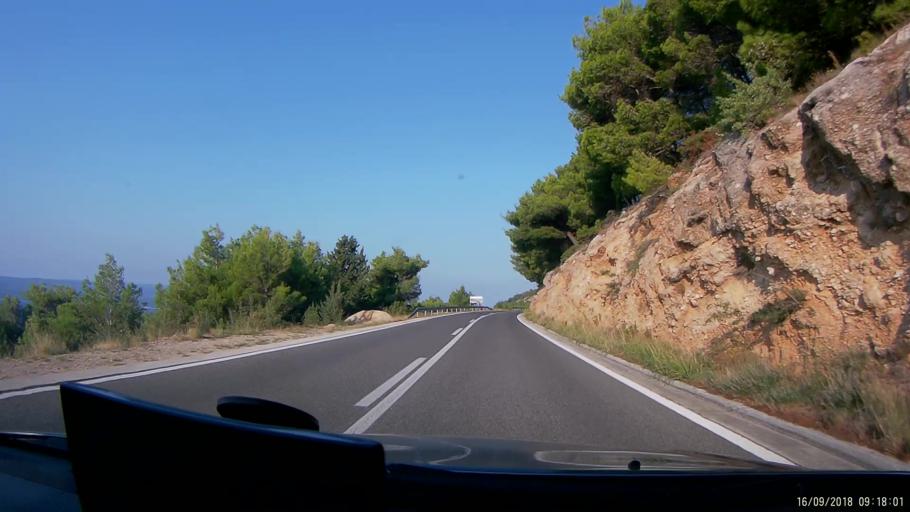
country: HR
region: Splitsko-Dalmatinska
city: Donja Brela
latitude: 43.4035
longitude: 16.8487
